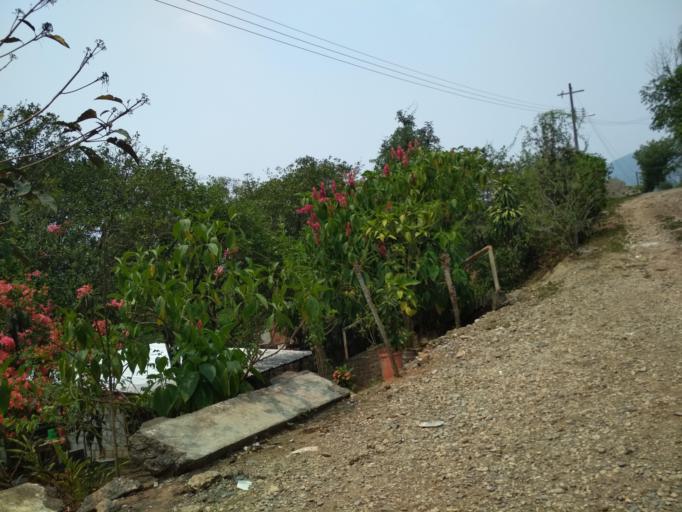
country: MX
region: Veracruz
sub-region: Tezonapa
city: Laguna Chica (Pueblo Nuevo)
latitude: 18.5480
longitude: -96.7322
